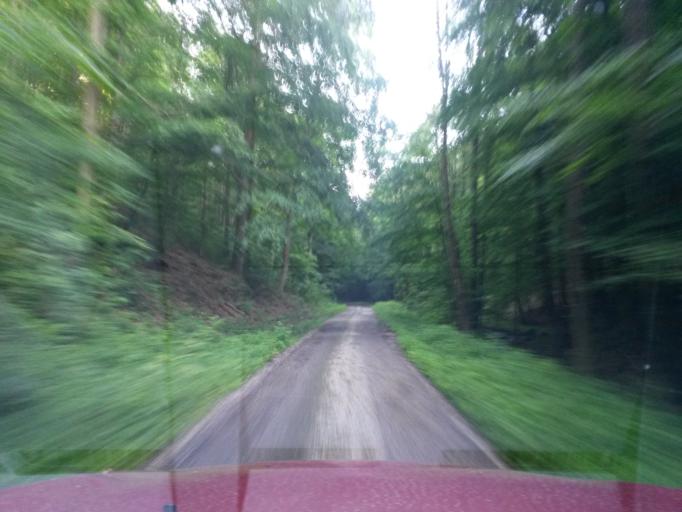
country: SK
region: Kosicky
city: Moldava nad Bodvou
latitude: 48.7355
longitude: 21.0647
